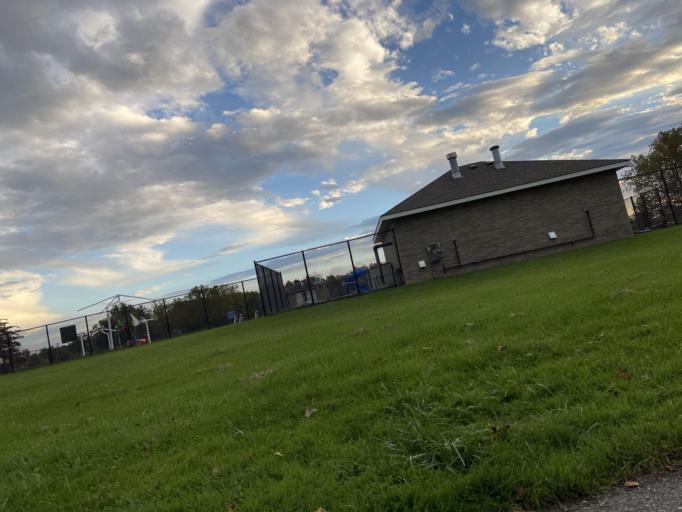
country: US
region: Michigan
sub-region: Wayne County
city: Livonia
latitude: 42.3646
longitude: -83.3248
